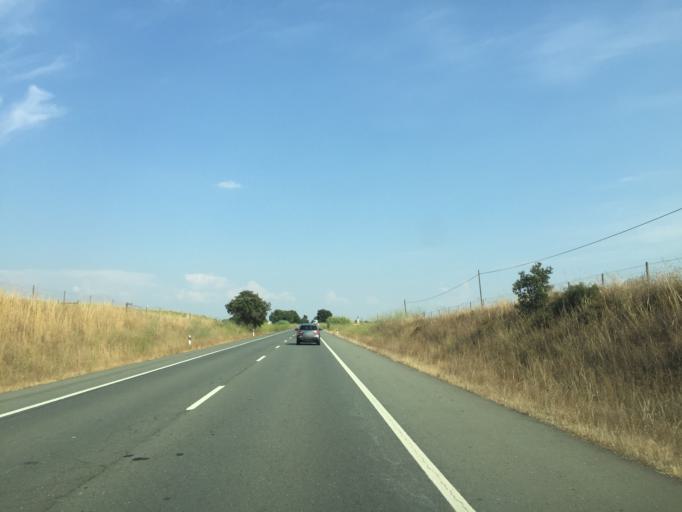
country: PT
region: Beja
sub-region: Aljustrel
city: Aljustrel
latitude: 37.9389
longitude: -8.3684
